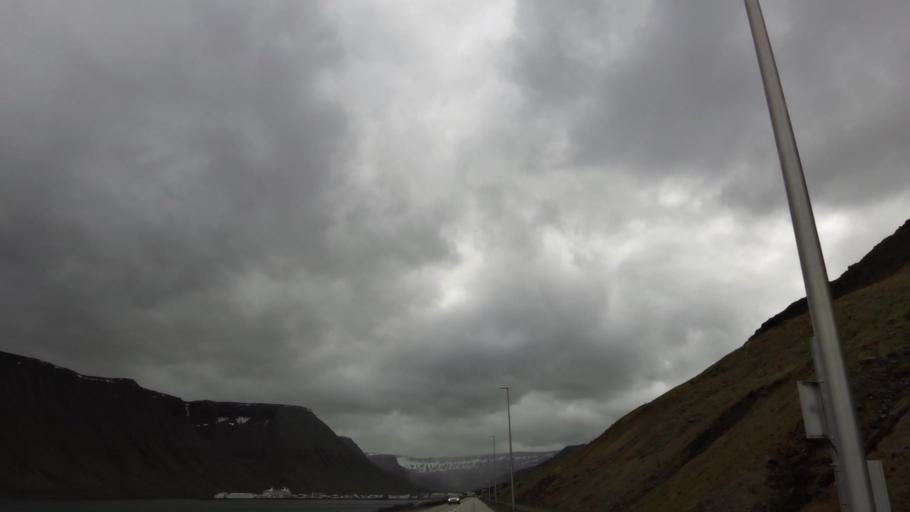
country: IS
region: Westfjords
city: Isafjoerdur
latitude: 66.0904
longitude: -23.1156
